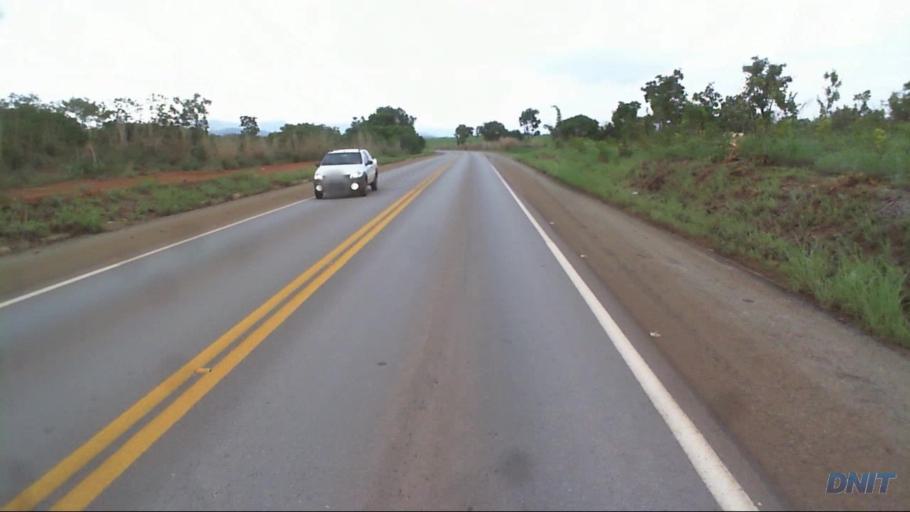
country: BR
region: Goias
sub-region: Barro Alto
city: Barro Alto
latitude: -14.7870
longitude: -49.0541
